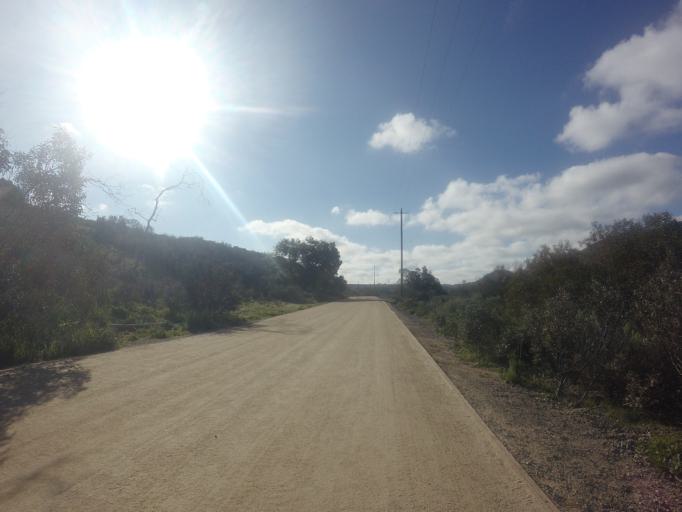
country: US
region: California
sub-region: Orange County
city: Foothill Ranch
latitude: 33.7705
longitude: -117.6802
